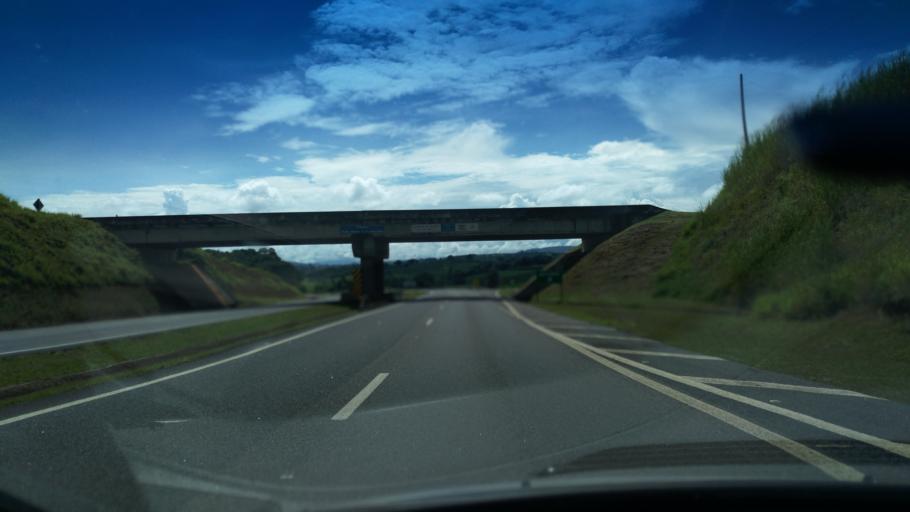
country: BR
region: Sao Paulo
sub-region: Santo Antonio Do Jardim
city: Espirito Santo do Pinhal
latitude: -22.2406
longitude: -46.8016
